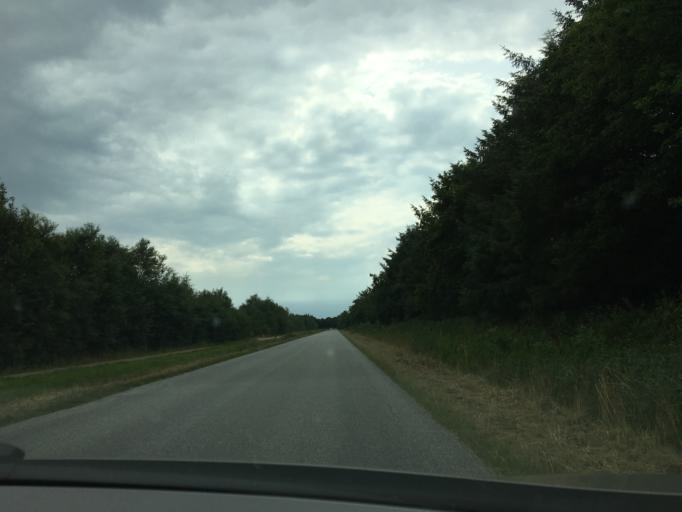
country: DK
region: South Denmark
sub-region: Varde Kommune
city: Oksbol
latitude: 55.8380
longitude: 8.2872
